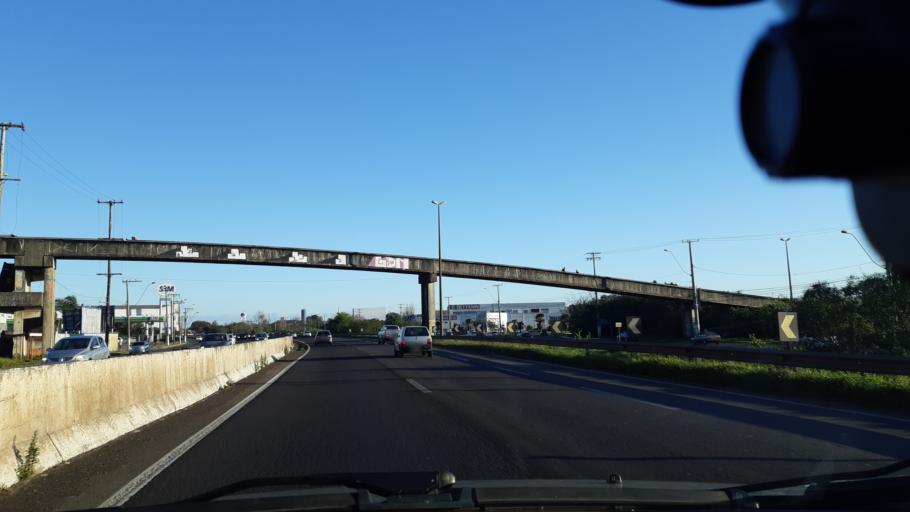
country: BR
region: Rio Grande do Sul
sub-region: Esteio
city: Esteio
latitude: -29.8590
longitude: -51.1809
